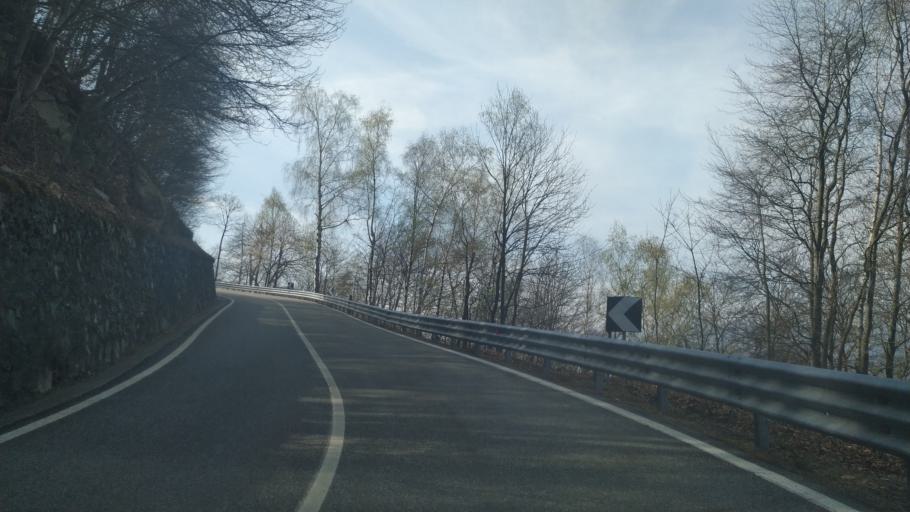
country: IT
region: Piedmont
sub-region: Provincia di Vercelli
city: Civiasco
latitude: 45.8089
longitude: 8.3061
